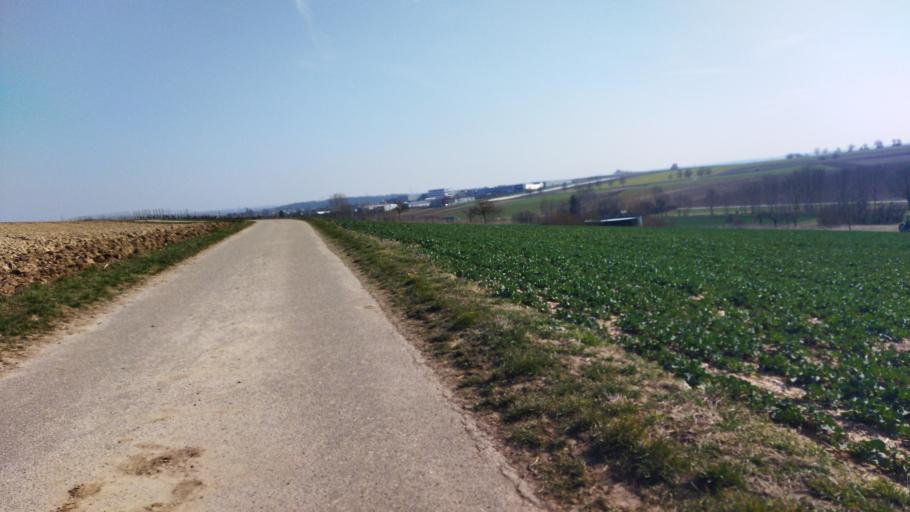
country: DE
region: Baden-Wuerttemberg
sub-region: Regierungsbezirk Stuttgart
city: Brackenheim
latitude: 49.0880
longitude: 9.0832
